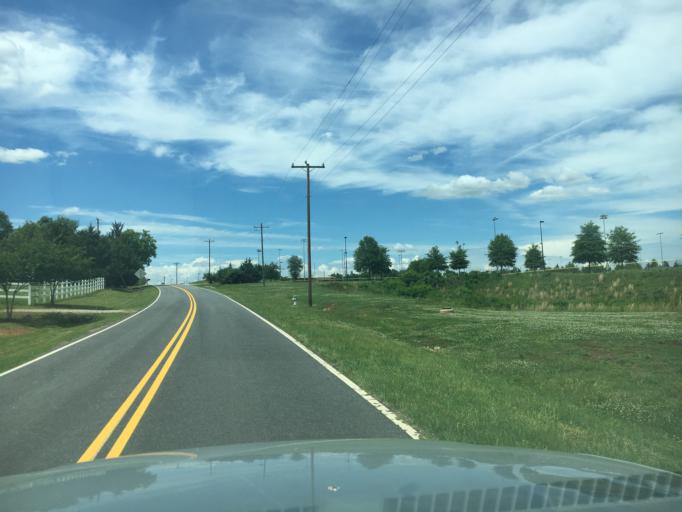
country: US
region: South Carolina
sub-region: Spartanburg County
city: Duncan
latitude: 34.8679
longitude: -82.1064
